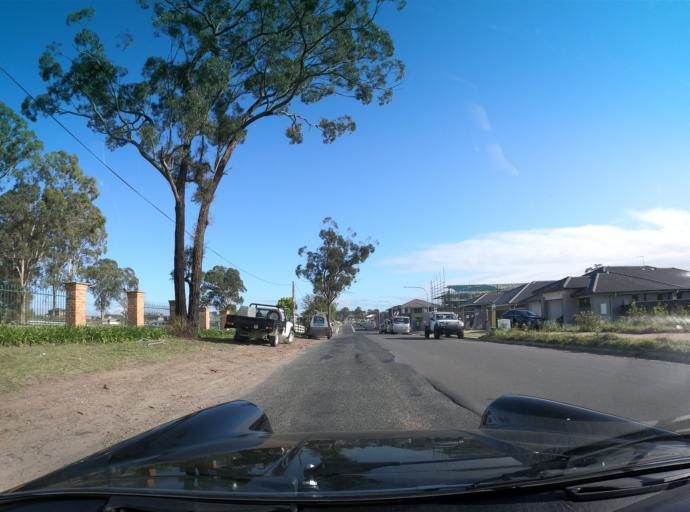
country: AU
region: New South Wales
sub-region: The Hills Shire
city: Beaumont Hills
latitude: -33.6921
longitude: 150.9616
